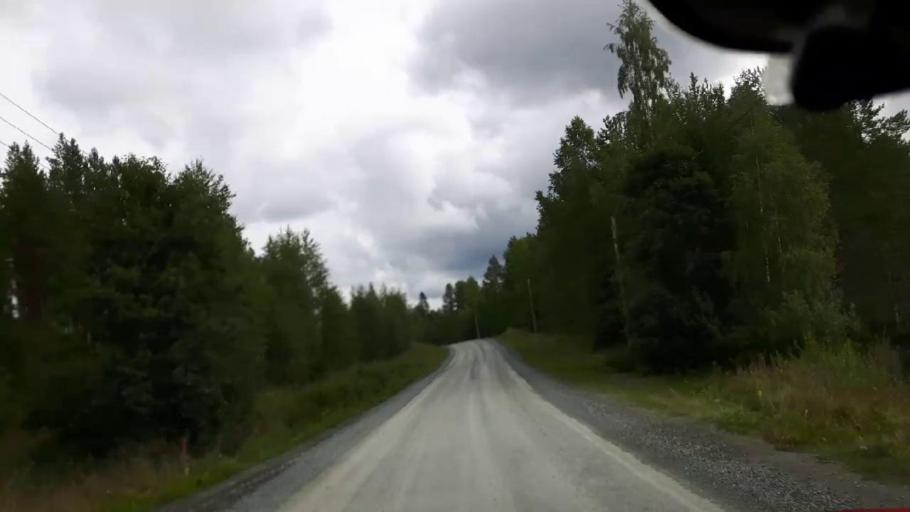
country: SE
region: Jaemtland
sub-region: Krokoms Kommun
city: Krokom
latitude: 63.5797
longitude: 14.2020
